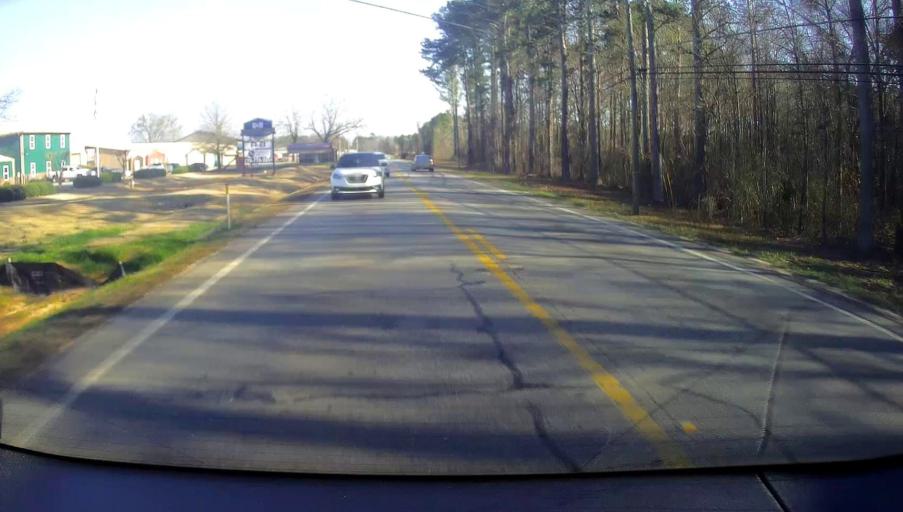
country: US
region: Georgia
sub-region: Butts County
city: Jackson
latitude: 33.2869
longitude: -83.9373
